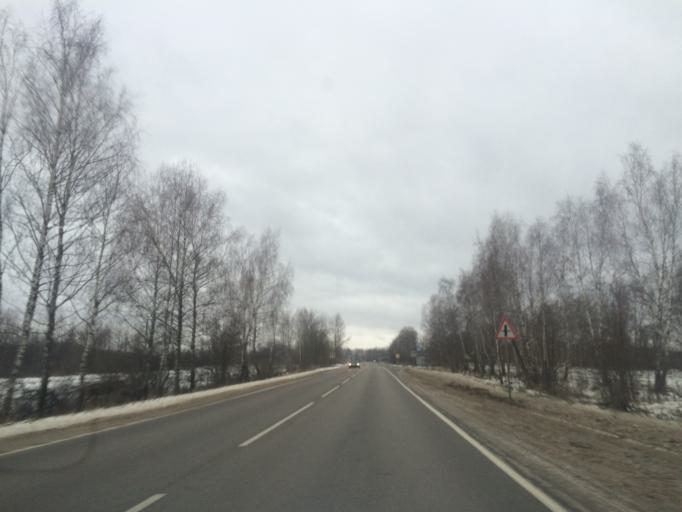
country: RU
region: Tula
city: Leninskiy
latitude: 54.1318
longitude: 37.3065
